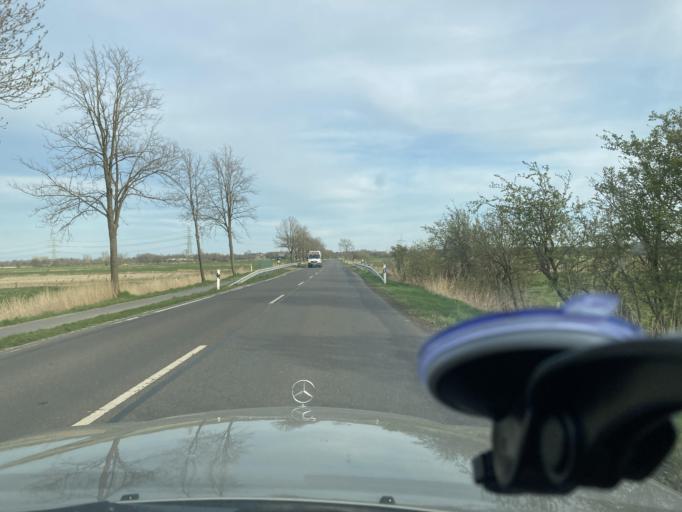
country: DE
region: Schleswig-Holstein
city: Stelle-Wittenwurth
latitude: 54.2496
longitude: 9.0677
